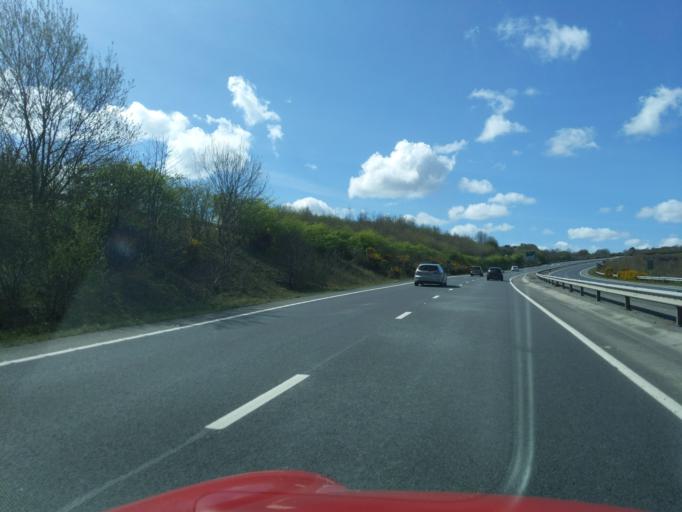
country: GB
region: England
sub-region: Cornwall
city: Liskeard
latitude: 50.4576
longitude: -4.5005
